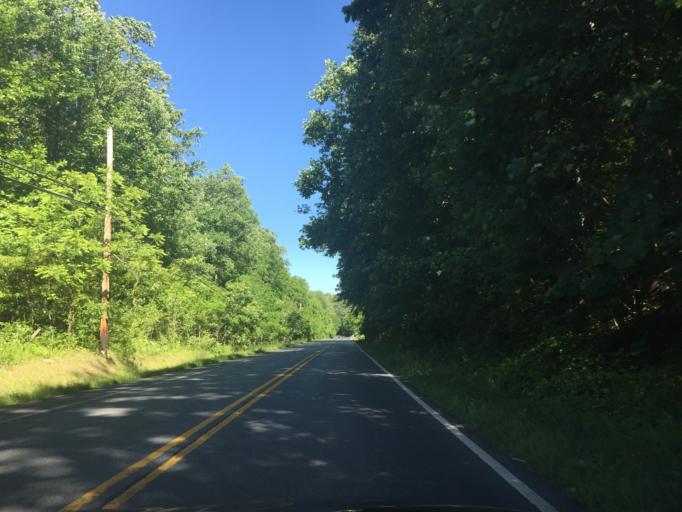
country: US
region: Maryland
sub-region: Carroll County
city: Westminster
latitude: 39.5690
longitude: -76.9551
